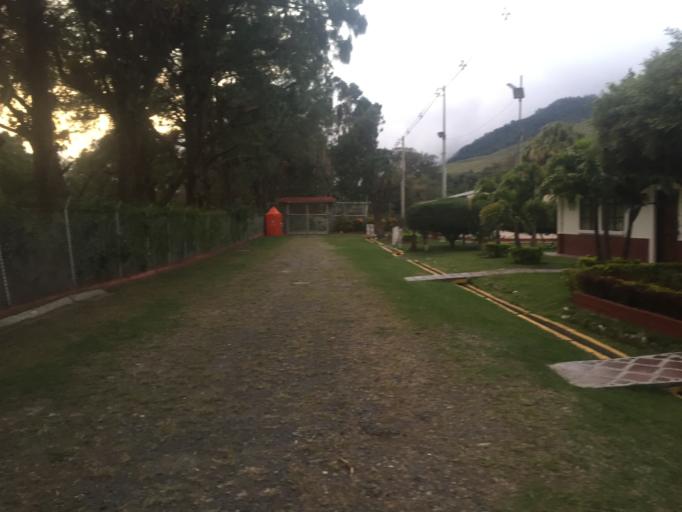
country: CO
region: Valle del Cauca
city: Calimita
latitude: 3.8808
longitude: -76.5384
